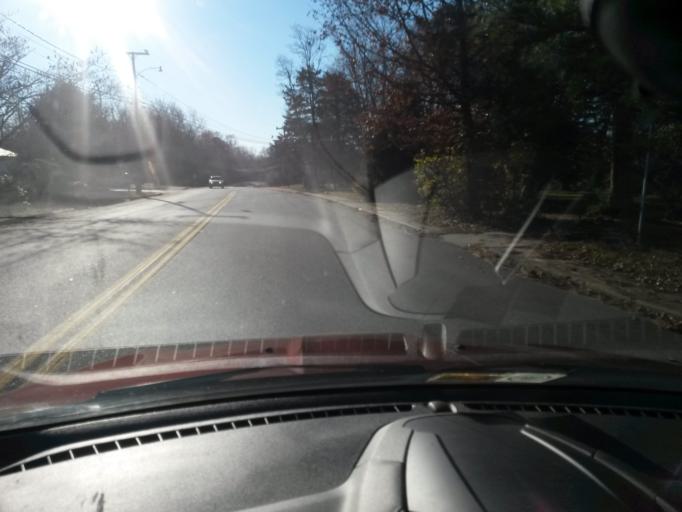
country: US
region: Virginia
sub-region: Appomattox County
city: Appomattox
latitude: 37.2620
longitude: -78.6819
